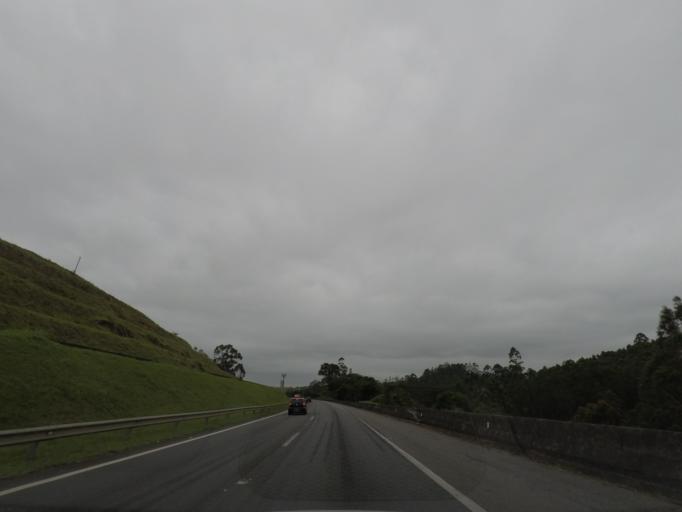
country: BR
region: Sao Paulo
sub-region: Jacarei
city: Jacarei
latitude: -23.2568
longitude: -46.0895
